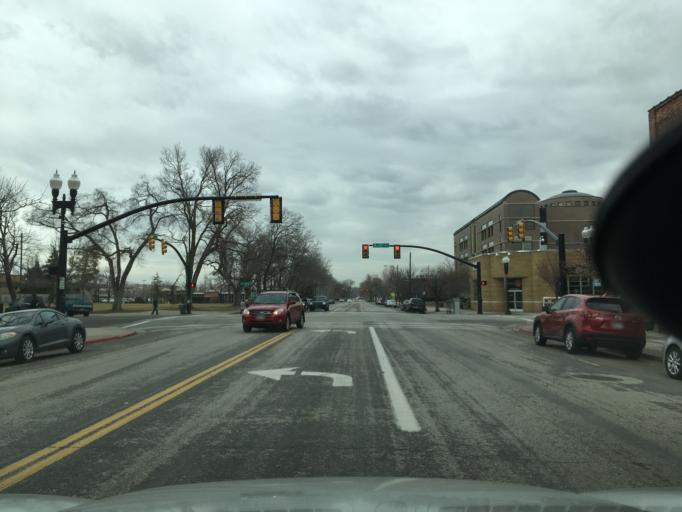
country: US
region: Utah
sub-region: Weber County
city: Ogden
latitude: 41.2211
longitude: -111.9733
